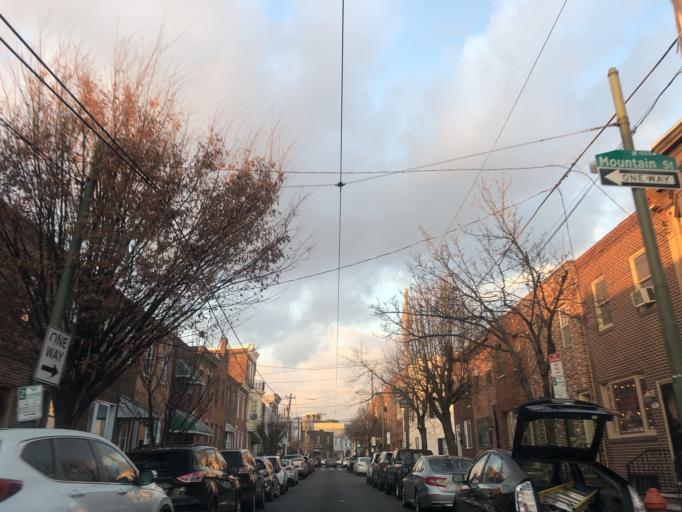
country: US
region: Pennsylvania
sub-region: Philadelphia County
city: Philadelphia
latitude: 39.9290
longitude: -75.1633
